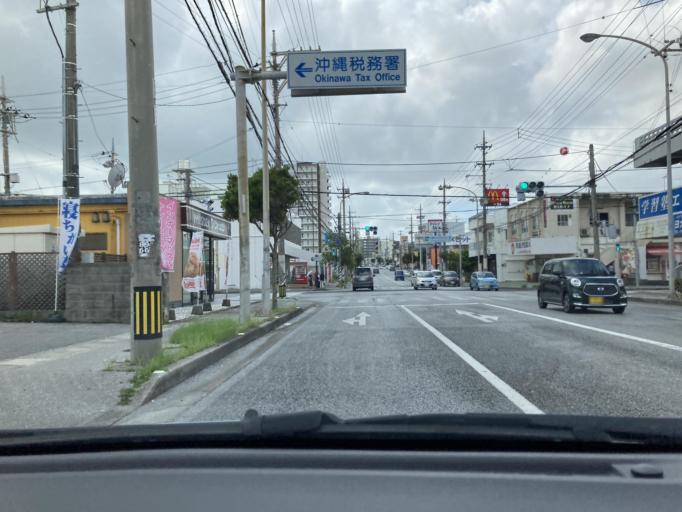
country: JP
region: Okinawa
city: Okinawa
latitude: 26.3454
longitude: 127.8218
